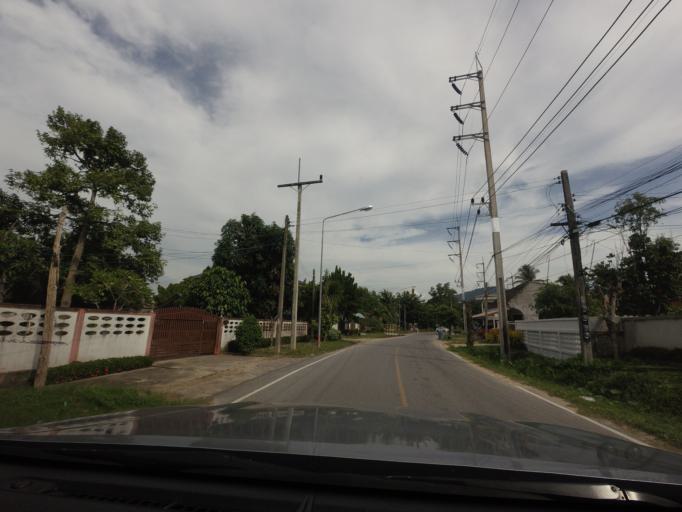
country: TH
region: Yala
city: Yala
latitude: 6.5162
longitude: 101.2894
